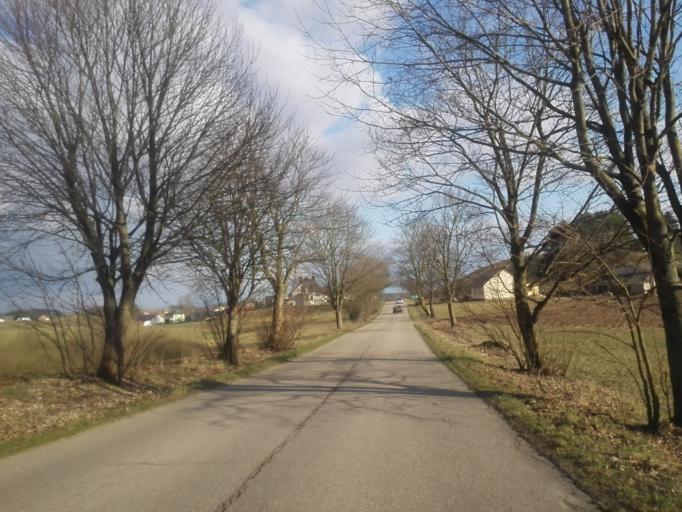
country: PL
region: Podlasie
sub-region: Suwalki
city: Suwalki
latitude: 54.2170
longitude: 22.8947
